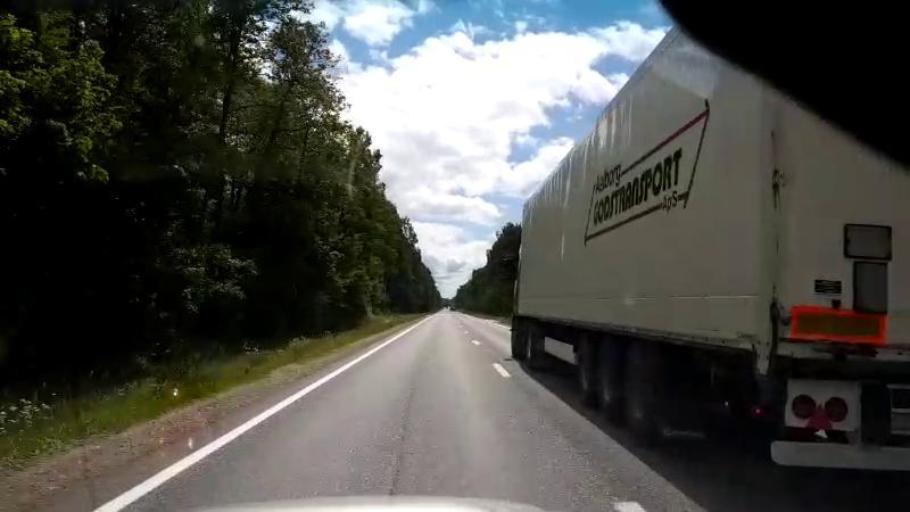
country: LV
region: Salacgrivas
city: Salacgriva
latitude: 57.5900
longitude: 24.4197
